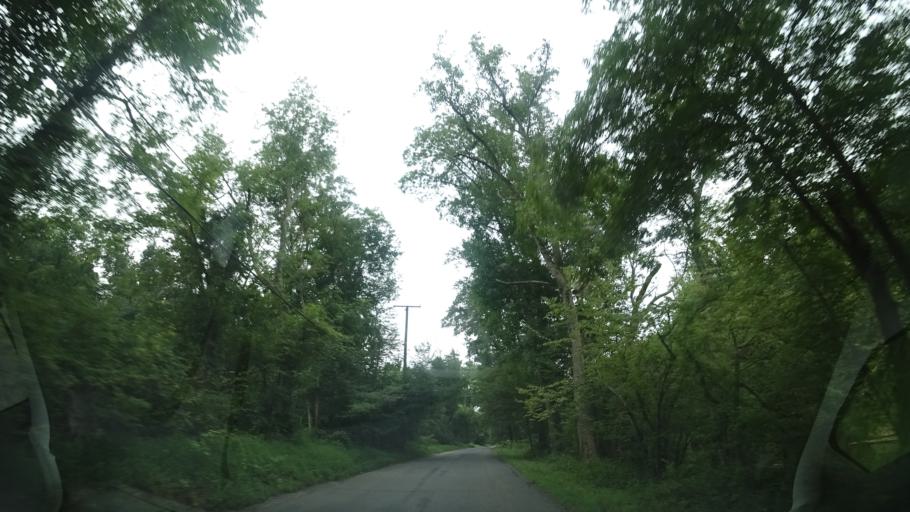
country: US
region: Virginia
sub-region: Loudoun County
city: Lowes Island
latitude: 39.0753
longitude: -77.3413
